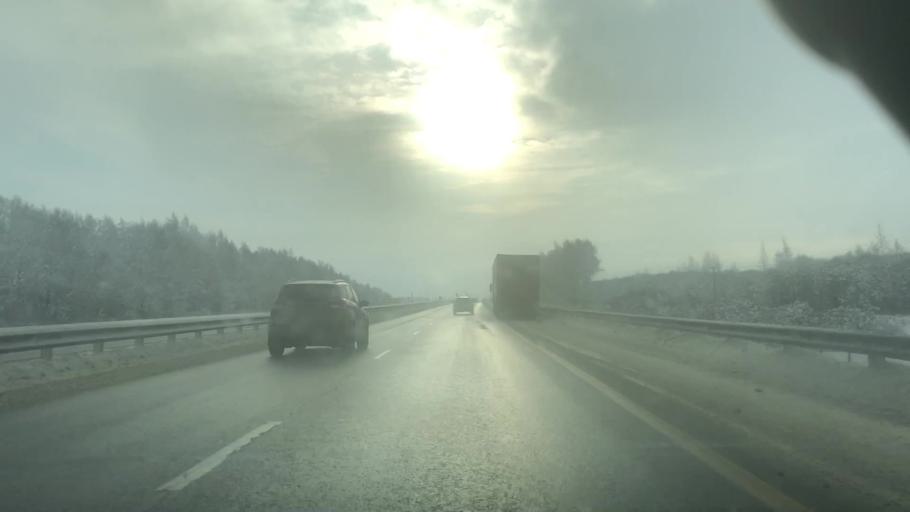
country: RU
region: Tula
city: Venev
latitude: 54.2865
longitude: 38.1589
